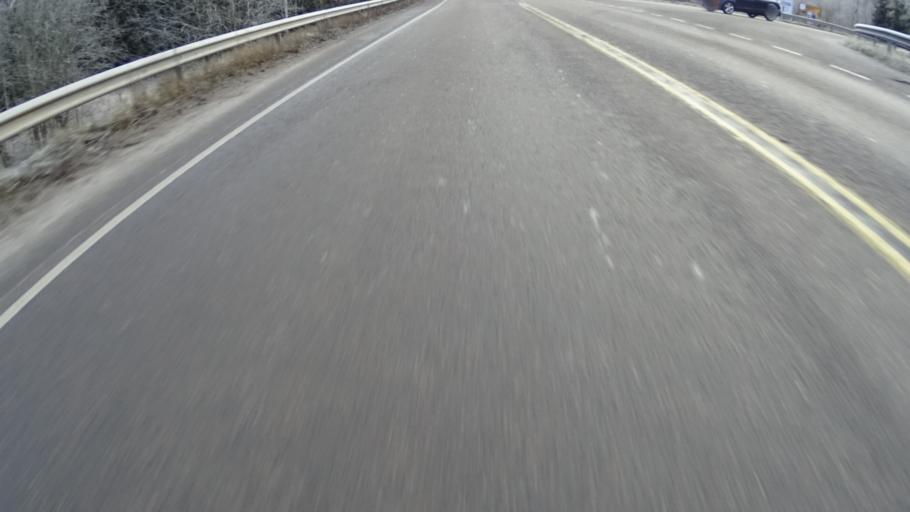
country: FI
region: Uusimaa
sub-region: Helsinki
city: Nurmijaervi
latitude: 60.3946
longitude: 24.7374
